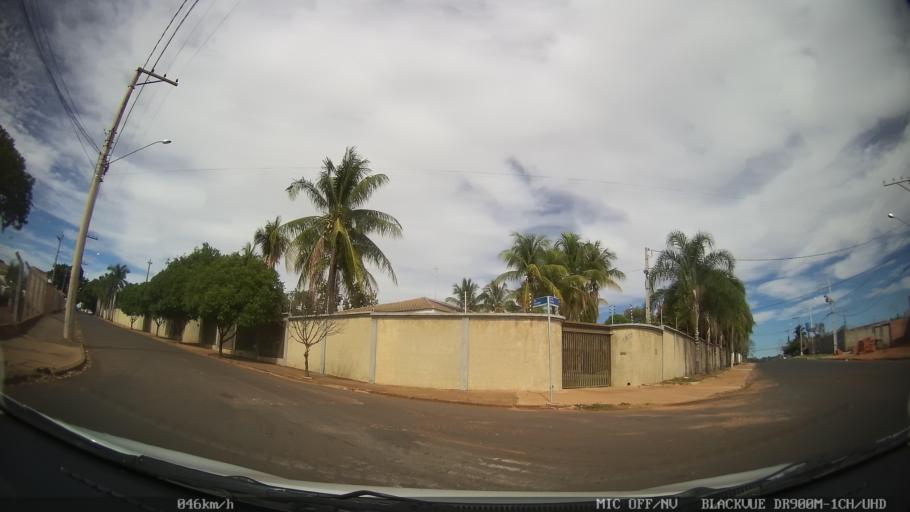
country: BR
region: Sao Paulo
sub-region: Catanduva
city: Catanduva
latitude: -21.1581
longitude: -48.9784
